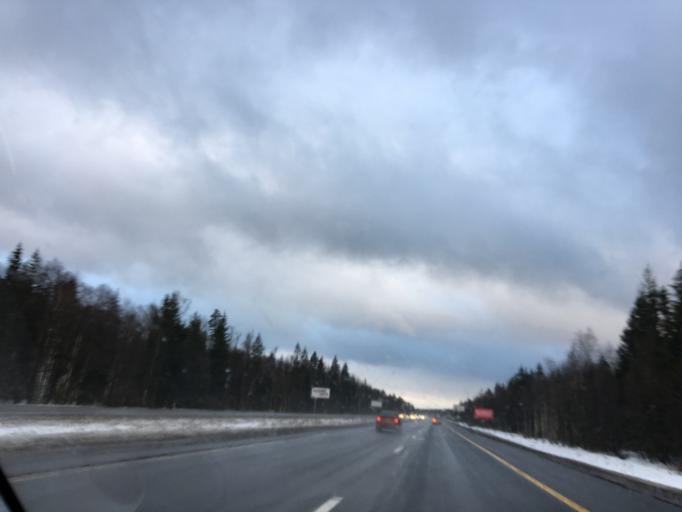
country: RU
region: Moskovskaya
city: Novyy Byt
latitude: 55.0035
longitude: 37.5478
